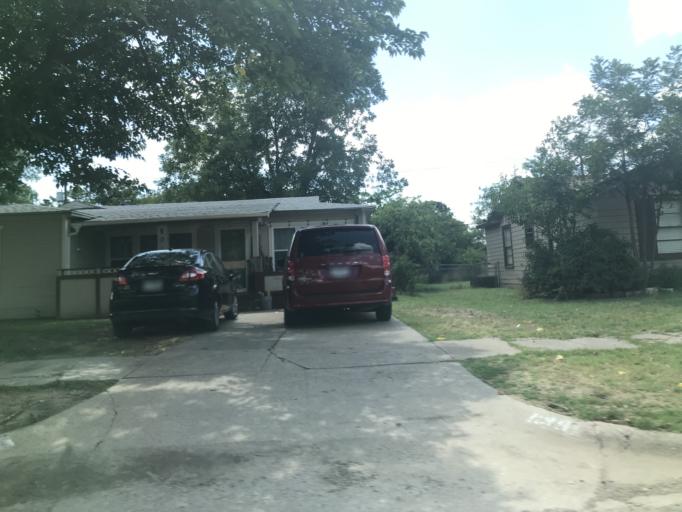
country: US
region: Texas
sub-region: Taylor County
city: Abilene
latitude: 32.4266
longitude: -99.7624
